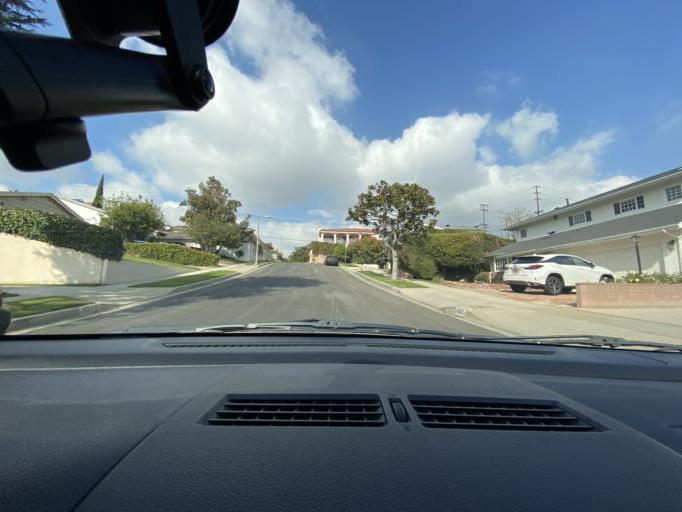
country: US
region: California
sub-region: Los Angeles County
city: Culver City
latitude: 34.0175
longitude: -118.4175
